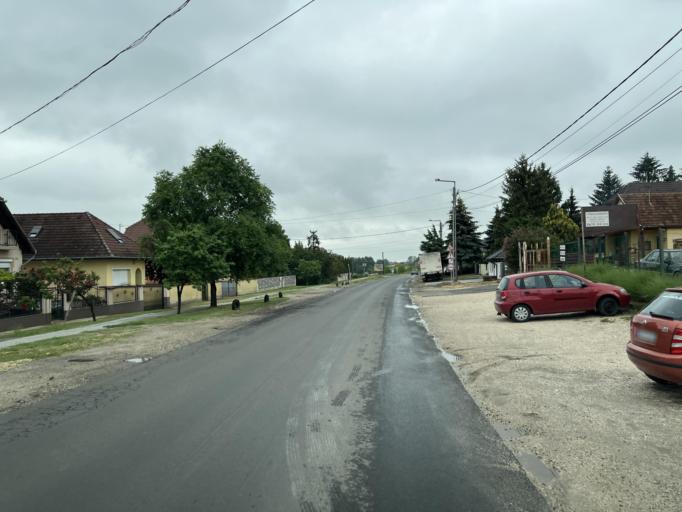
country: HU
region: Pest
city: Galgaheviz
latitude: 47.6182
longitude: 19.5729
